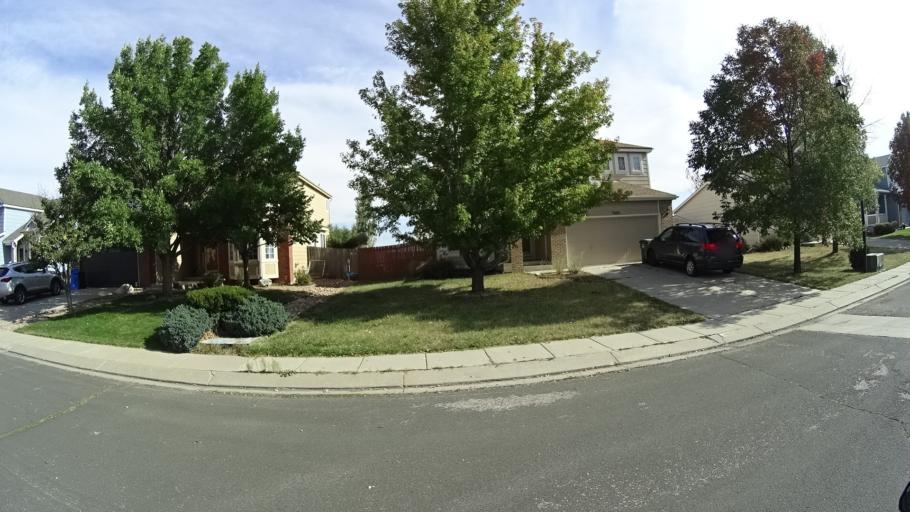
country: US
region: Colorado
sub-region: El Paso County
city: Cimarron Hills
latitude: 38.9040
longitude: -104.6896
